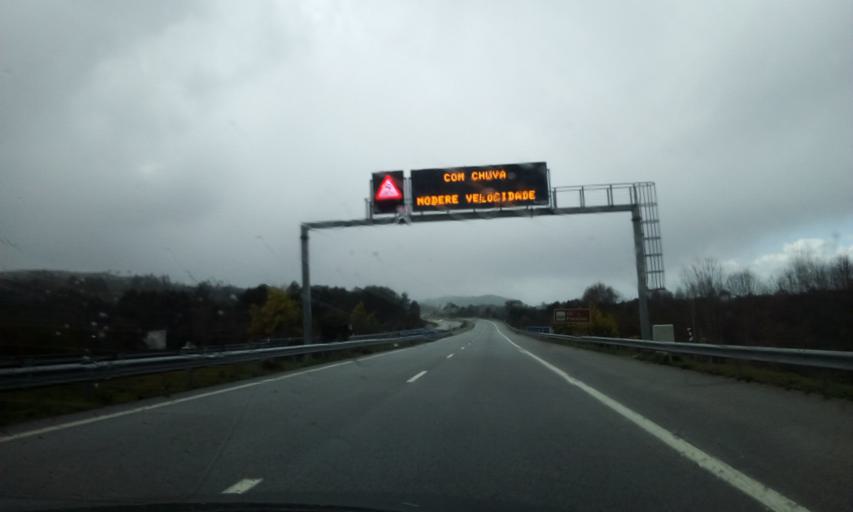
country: PT
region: Viseu
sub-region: Mangualde
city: Mangualde
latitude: 40.6141
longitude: -7.6825
